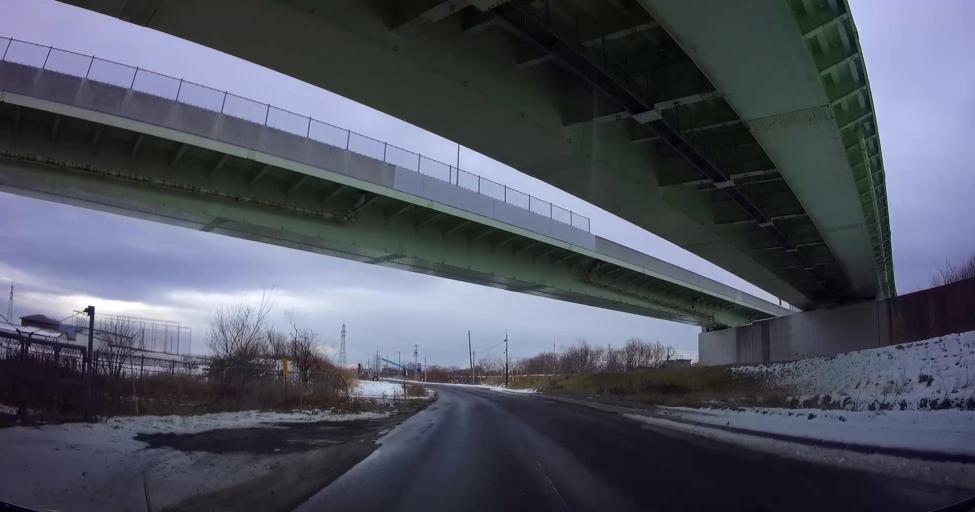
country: JP
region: Hokkaido
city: Kamiiso
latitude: 41.8340
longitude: 140.6900
